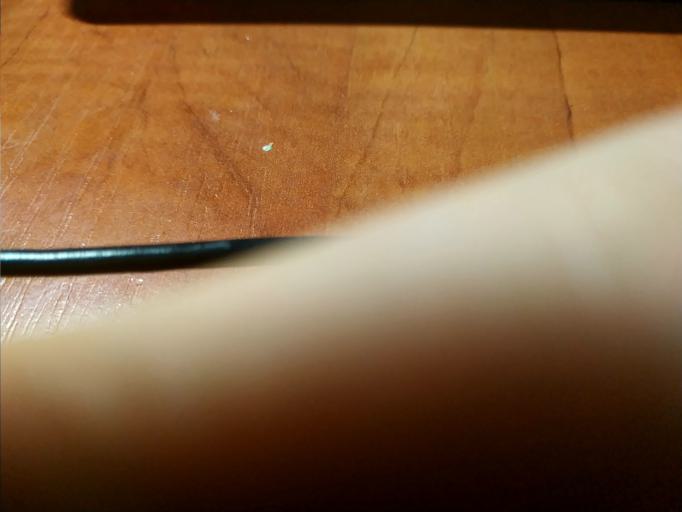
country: RU
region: Tverskaya
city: Likhoslavl'
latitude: 57.0252
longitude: 35.6140
